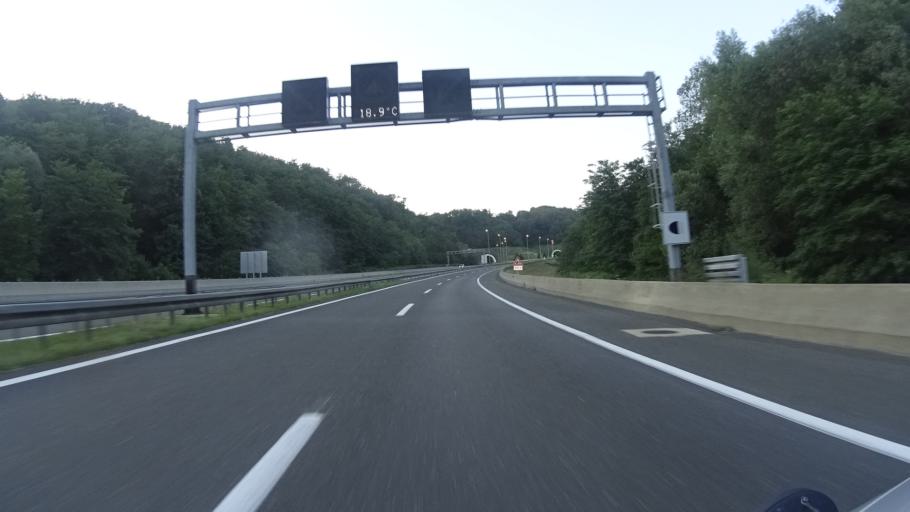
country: HR
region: Varazdinska
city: Ljubescica
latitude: 46.2158
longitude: 16.4043
